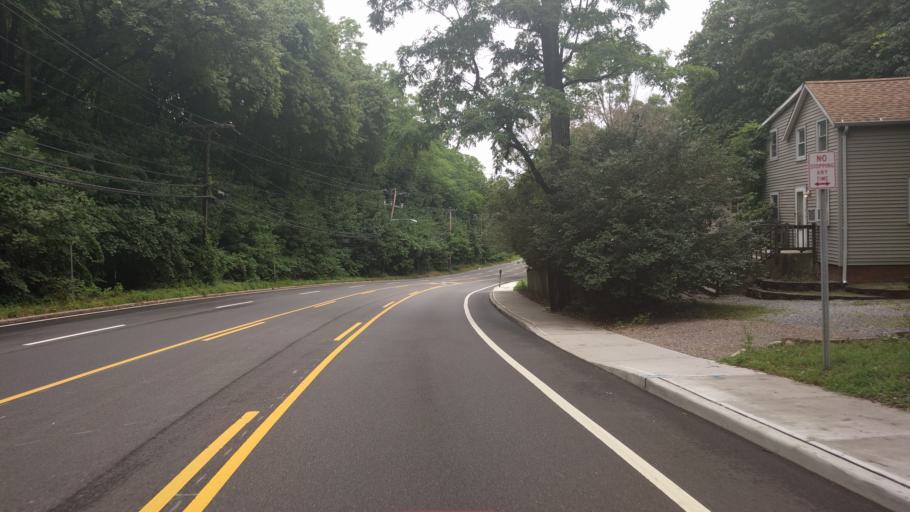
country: US
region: New York
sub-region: Suffolk County
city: Huntington
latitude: 40.8611
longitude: -73.4275
